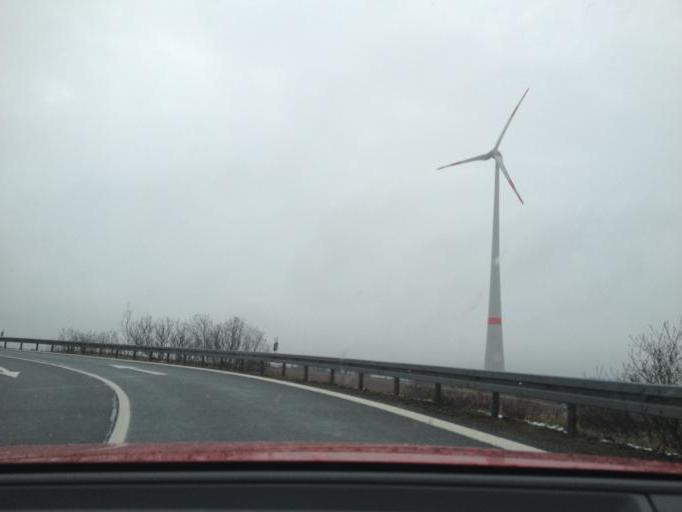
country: DE
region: Bavaria
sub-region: Upper Franconia
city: Gattendorf
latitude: 50.3101
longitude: 12.0212
